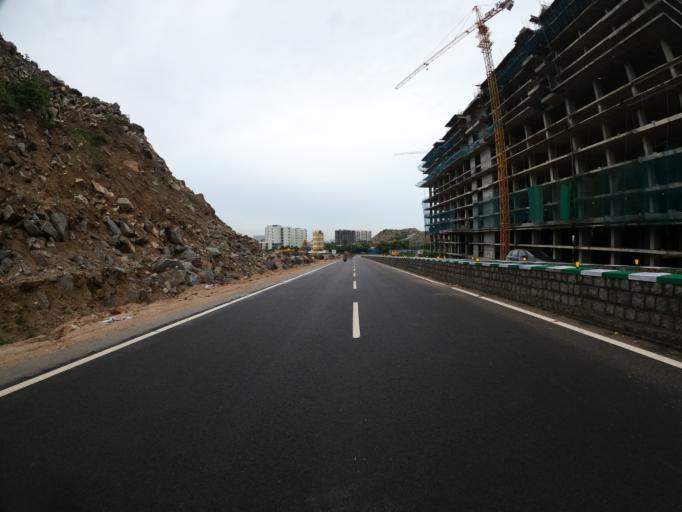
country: IN
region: Telangana
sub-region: Rangareddi
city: Kukatpalli
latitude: 17.4631
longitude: 78.3832
